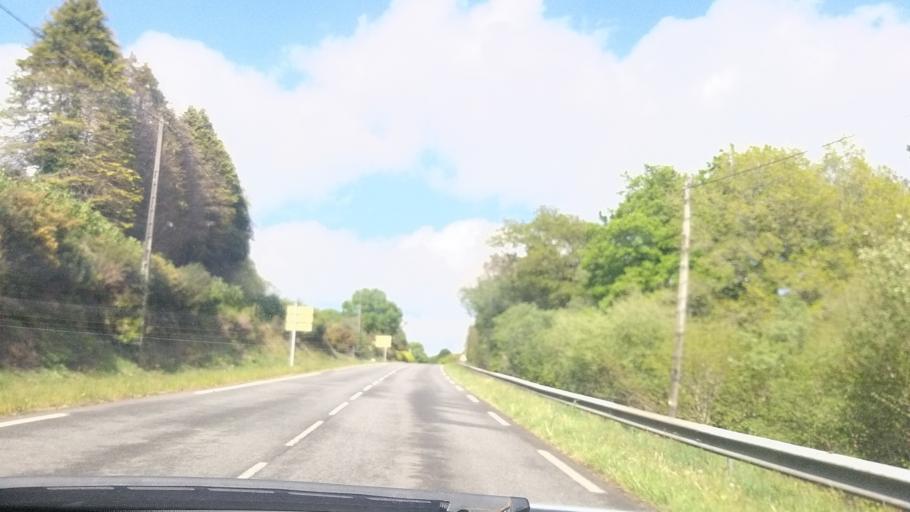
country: FR
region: Brittany
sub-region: Departement du Finistere
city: Huelgoat
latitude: 48.3449
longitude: -3.7550
